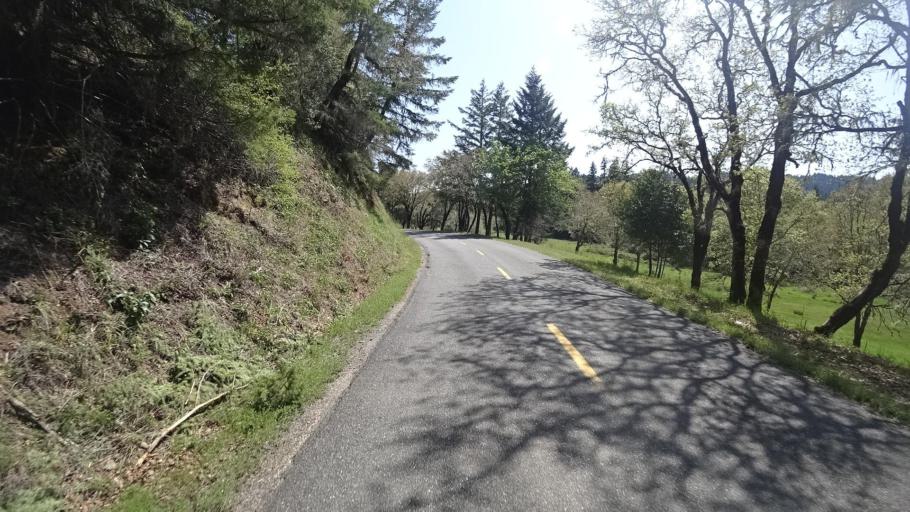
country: US
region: California
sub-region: Humboldt County
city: Redway
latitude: 40.3005
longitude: -123.6538
